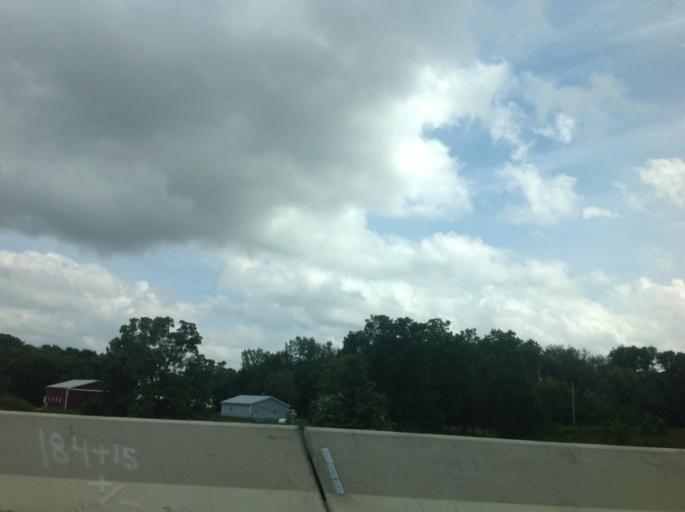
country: US
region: Ohio
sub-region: Morrow County
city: Mount Gilead
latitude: 40.4756
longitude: -82.7494
